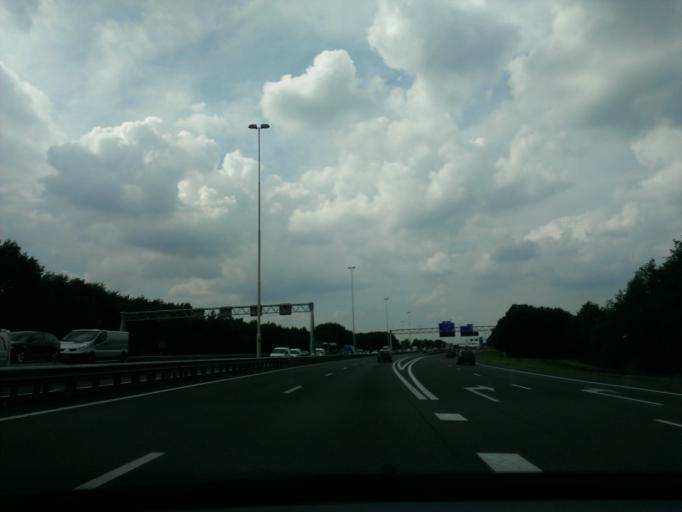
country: NL
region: Utrecht
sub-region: Gemeente Leusden
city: Leusden
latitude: 52.1683
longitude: 5.4442
